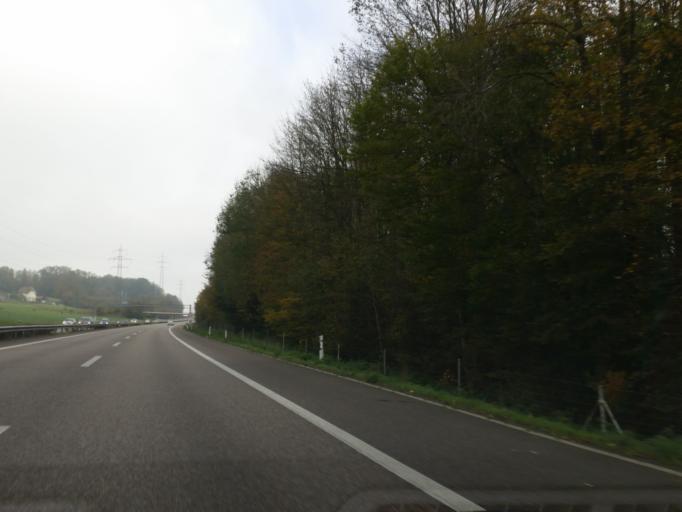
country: CH
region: Aargau
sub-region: Bezirk Zofingen
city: Safenwil
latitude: 47.3202
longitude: 7.9575
